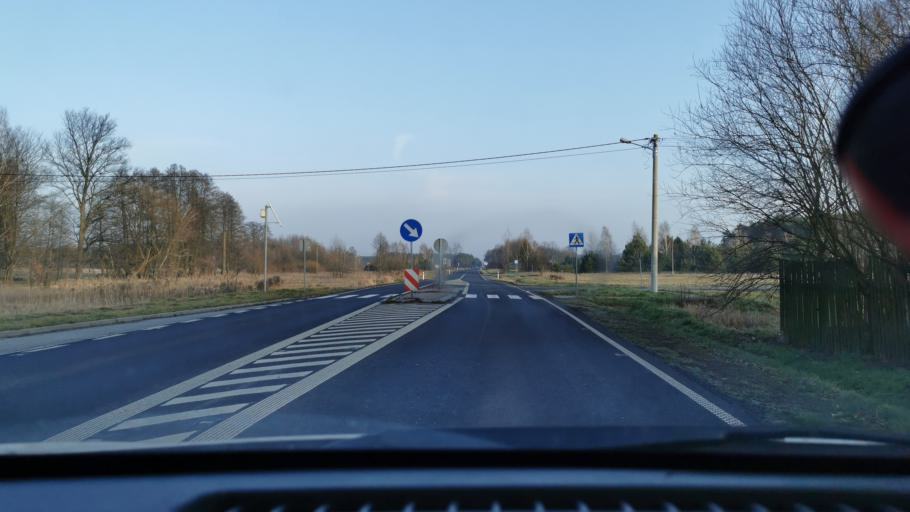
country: PL
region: Lodz Voivodeship
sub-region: Powiat pabianicki
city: Dlutow
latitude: 51.5123
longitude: 19.3363
